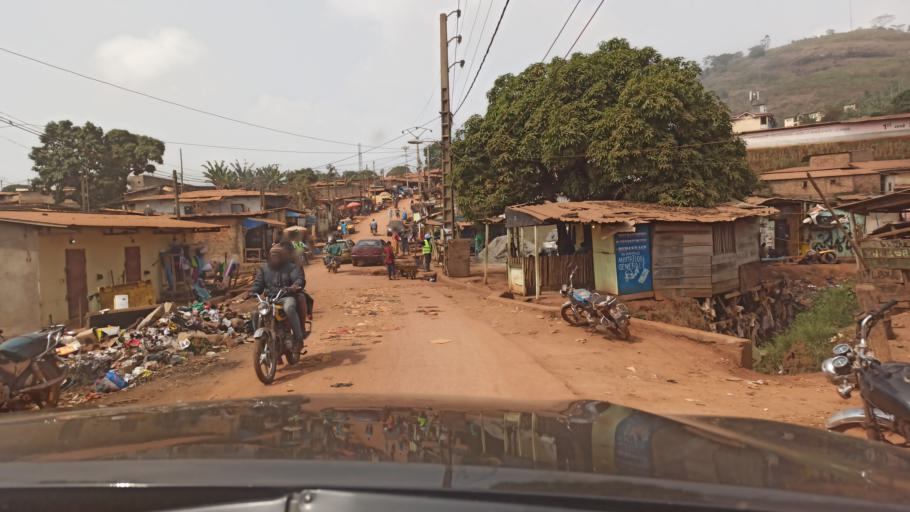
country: CM
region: Centre
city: Yaounde
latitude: 3.8854
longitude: 11.4902
